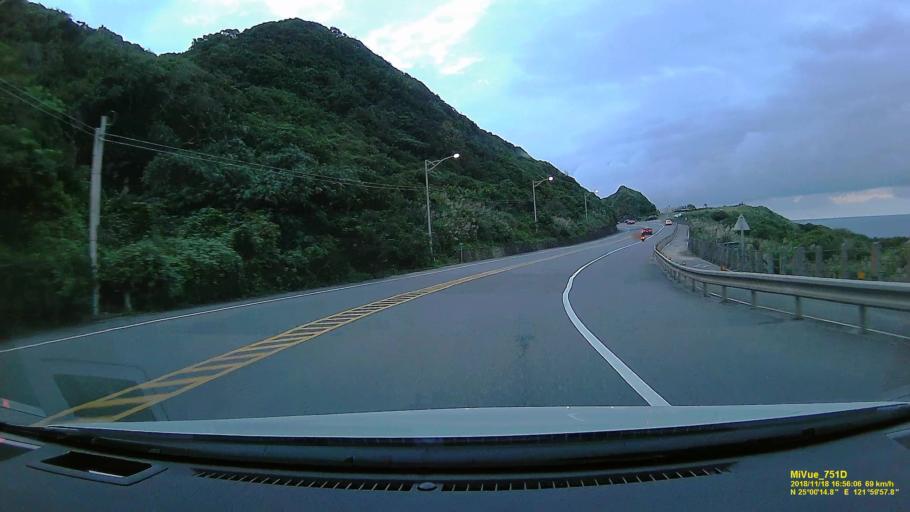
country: TW
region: Taiwan
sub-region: Keelung
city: Keelung
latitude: 25.0042
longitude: 121.9998
